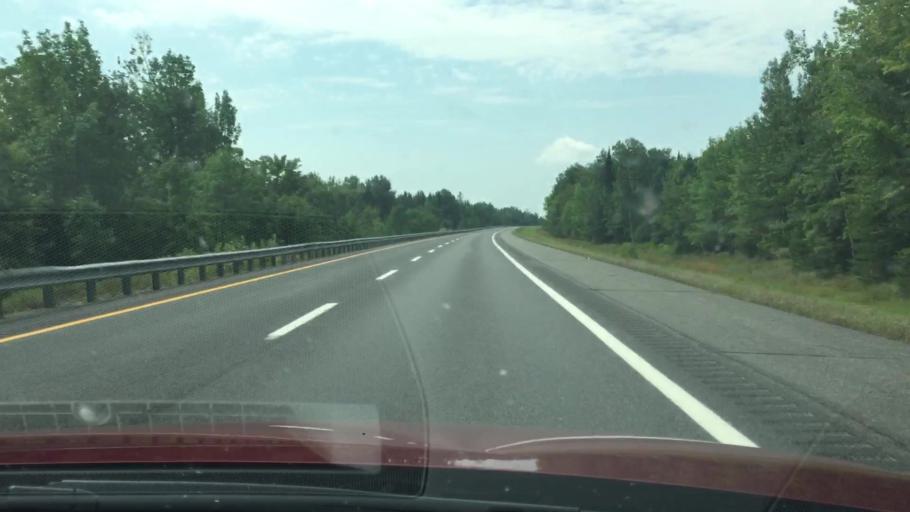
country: US
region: Maine
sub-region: Aroostook County
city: Hodgdon
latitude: 46.1243
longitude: -68.1080
